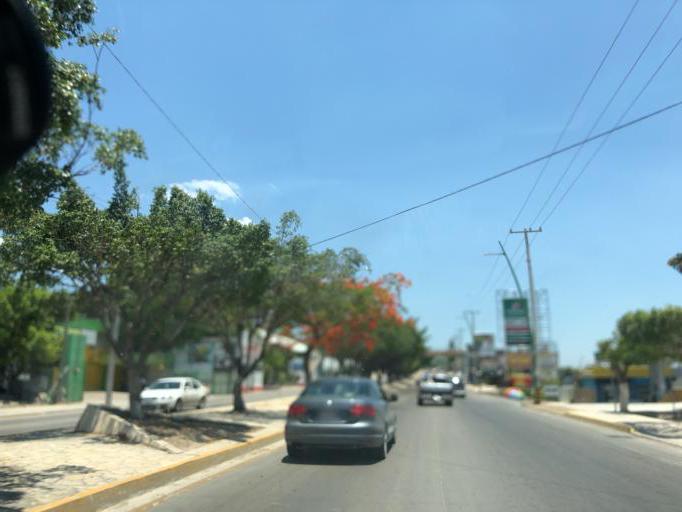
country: MX
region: Chiapas
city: Tuxtla Gutierrez
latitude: 16.7448
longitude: -93.1311
